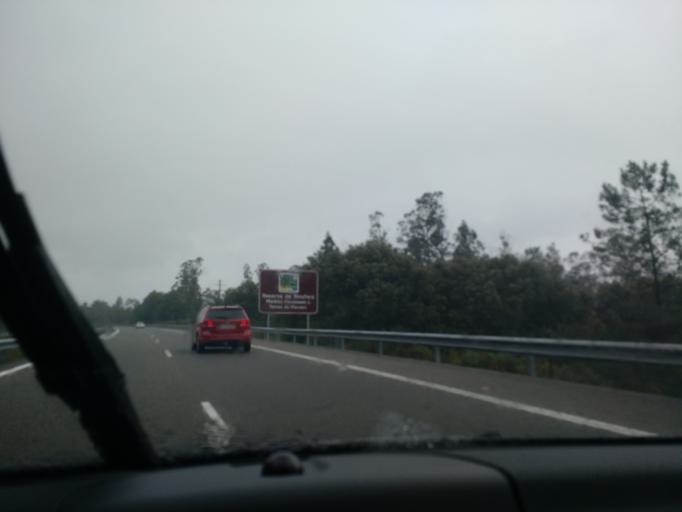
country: ES
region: Galicia
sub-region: Provincia da Coruna
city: Mesia
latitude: 43.1497
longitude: -8.3281
